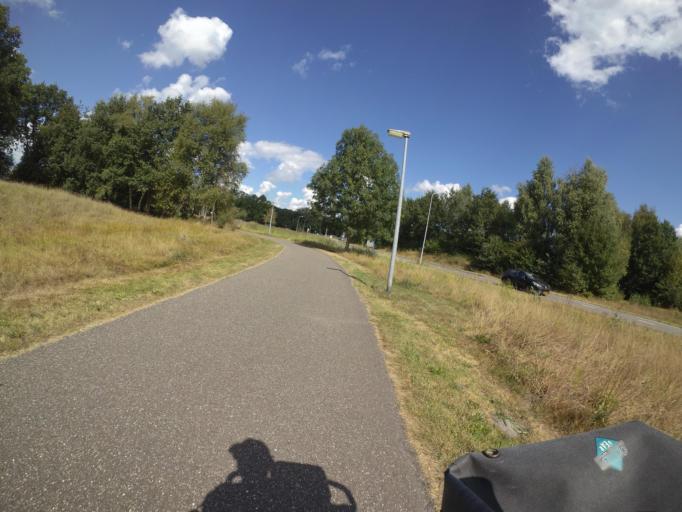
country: NL
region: Groningen
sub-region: Gemeente Leek
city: Leek
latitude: 53.1397
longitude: 6.4117
